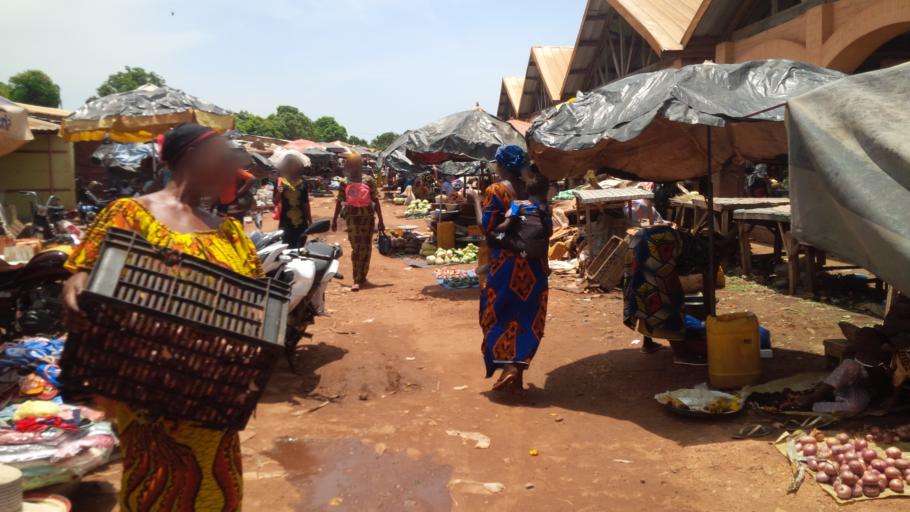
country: CI
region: Savanes
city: Korhogo
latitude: 9.4699
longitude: -5.6354
